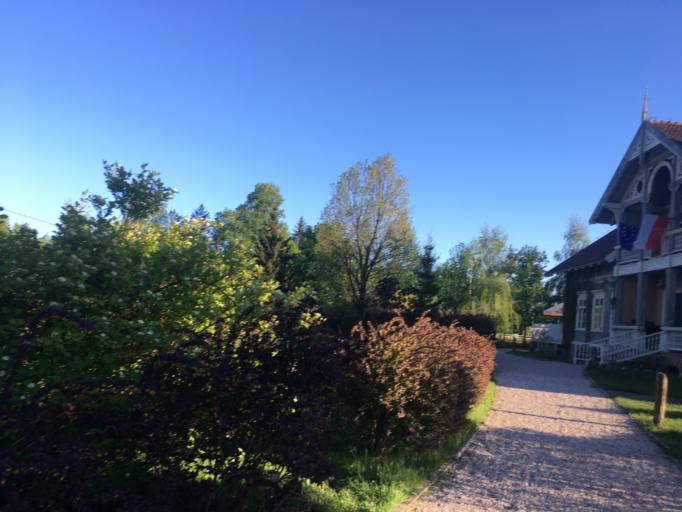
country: PL
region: Warmian-Masurian Voivodeship
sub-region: Powiat piski
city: Ruciane-Nida
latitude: 53.6886
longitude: 21.4691
